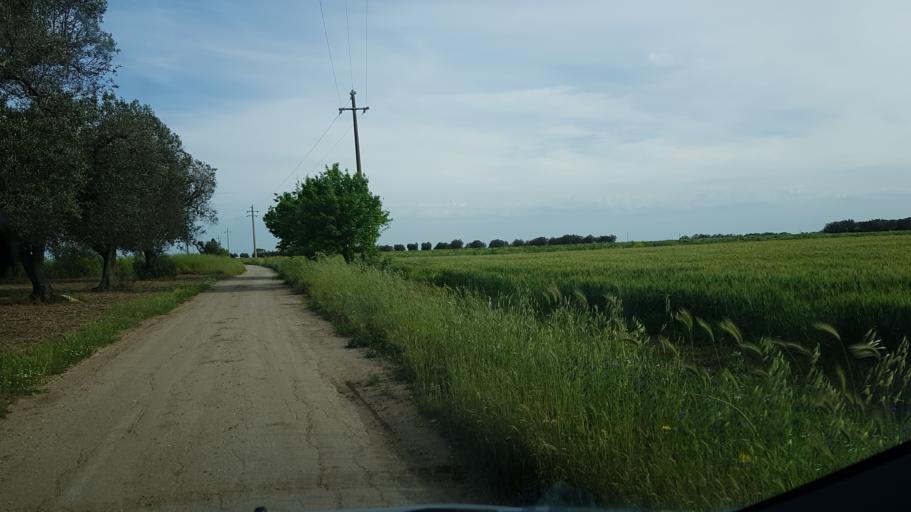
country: IT
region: Apulia
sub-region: Provincia di Brindisi
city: Tuturano
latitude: 40.5106
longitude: 17.9624
